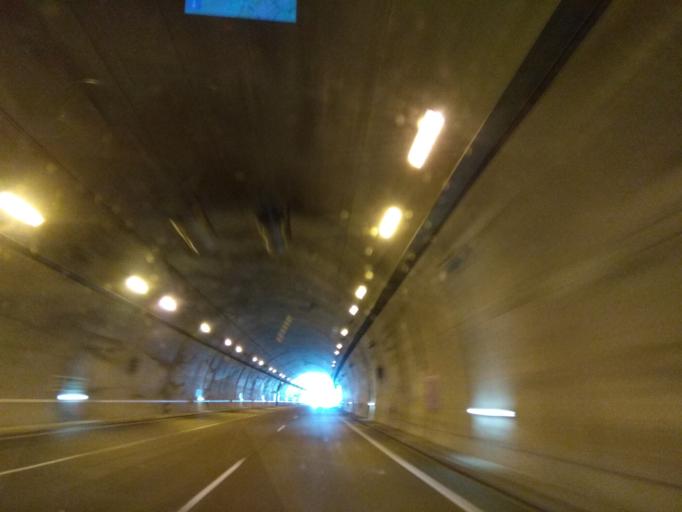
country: ES
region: Castille and Leon
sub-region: Provincia de Burgos
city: Burgos
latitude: 42.3823
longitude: -3.6720
